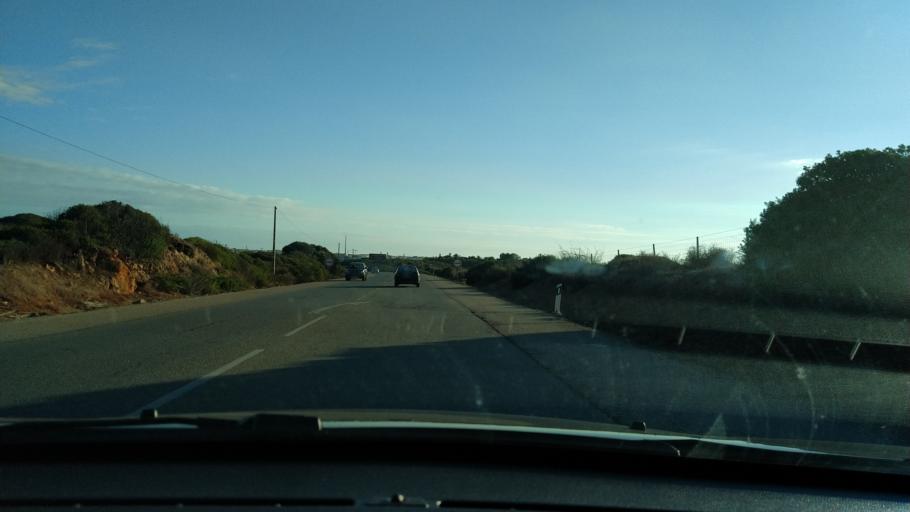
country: PT
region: Faro
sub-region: Vila do Bispo
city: Sagres
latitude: 37.0267
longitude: -8.9373
